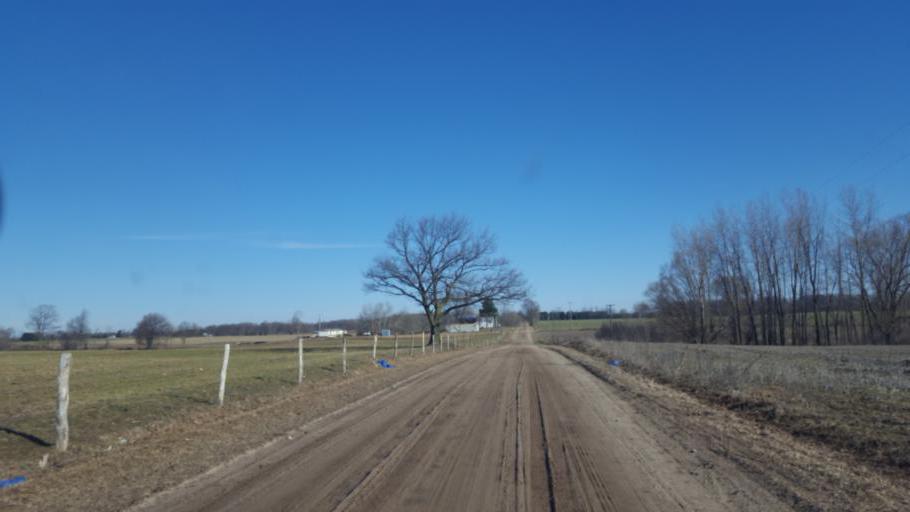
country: US
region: Michigan
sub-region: Montcalm County
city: Edmore
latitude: 43.4999
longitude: -85.0652
